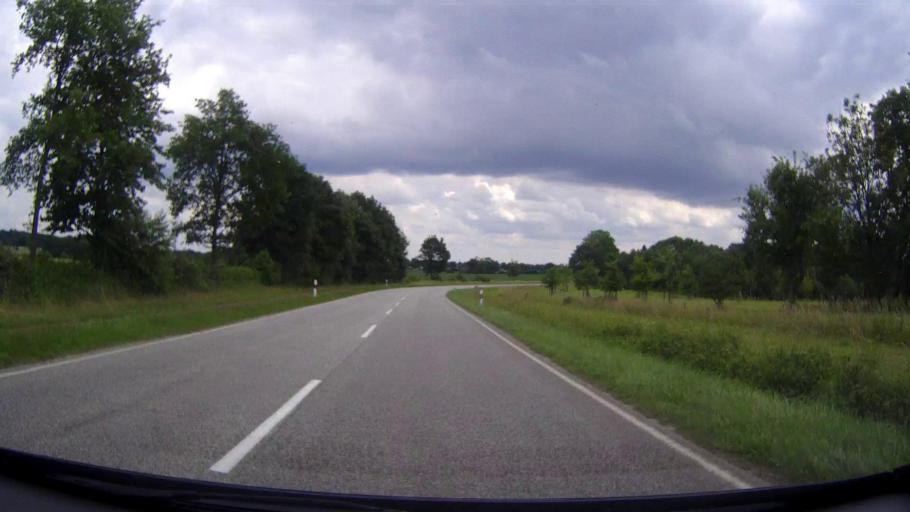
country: DE
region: Schleswig-Holstein
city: Warringholz
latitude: 54.0699
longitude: 9.4699
